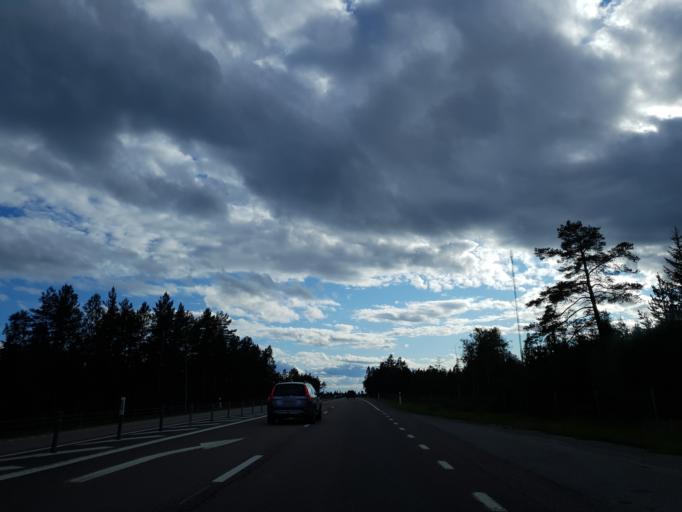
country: SE
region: Vaesternorrland
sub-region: Haernoesands Kommun
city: Haernoesand
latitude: 62.5688
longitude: 17.7382
